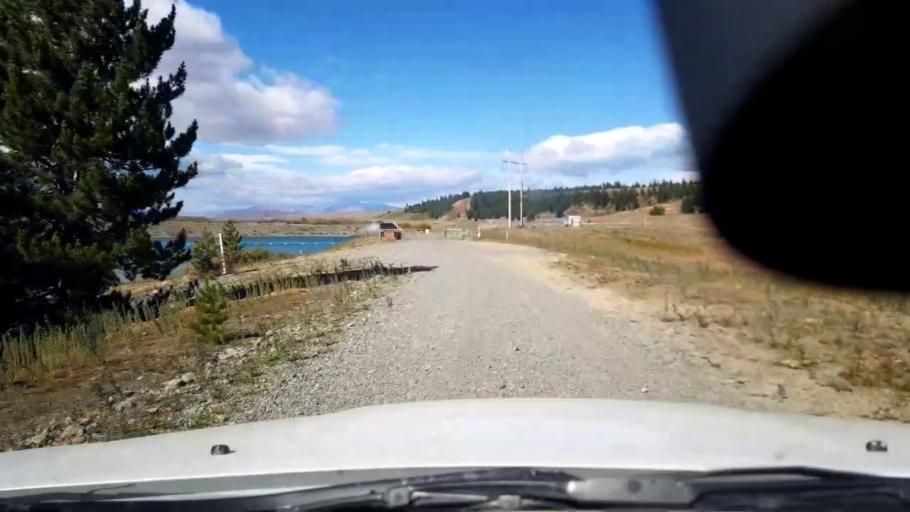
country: NZ
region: Canterbury
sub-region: Timaru District
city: Pleasant Point
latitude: -44.0136
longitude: 170.4639
